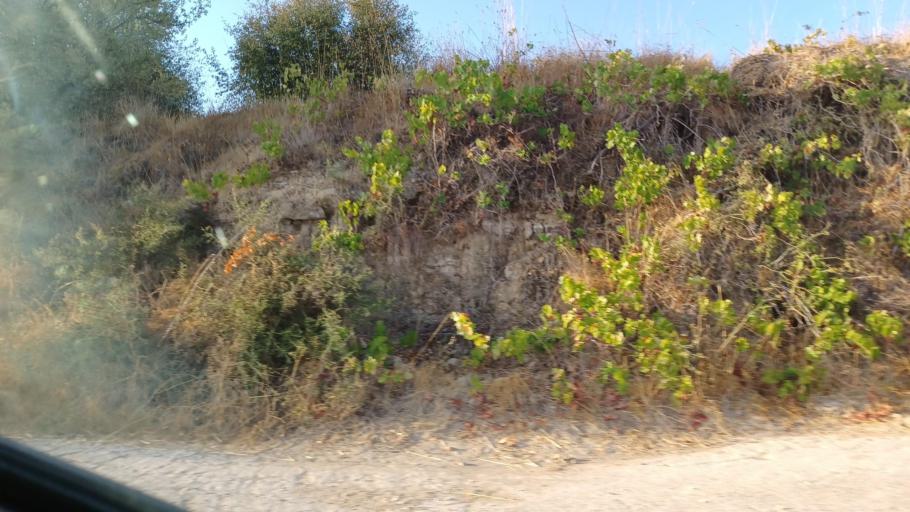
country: CY
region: Pafos
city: Tala
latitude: 34.9218
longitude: 32.5010
